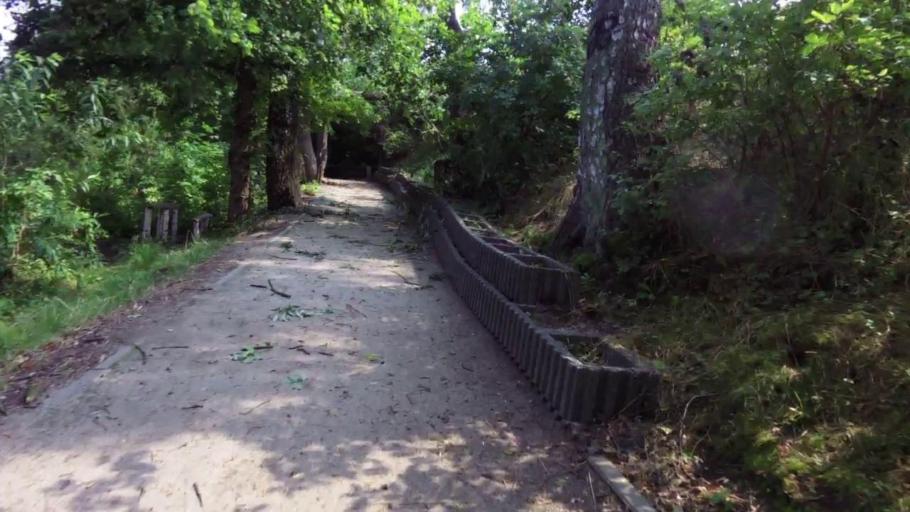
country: PL
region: West Pomeranian Voivodeship
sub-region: Powiat choszczenski
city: Choszczno
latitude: 53.1581
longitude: 15.4191
